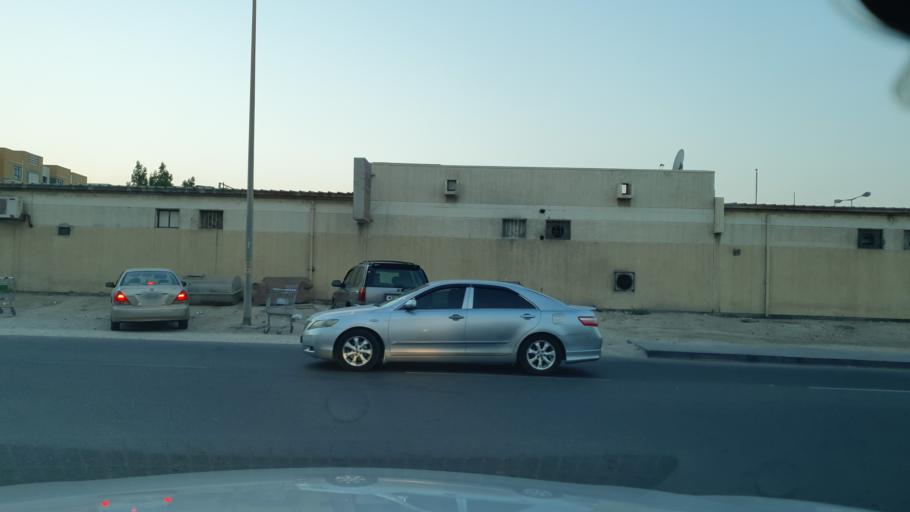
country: BH
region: Northern
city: Madinat `Isa
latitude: 26.1710
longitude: 50.5530
